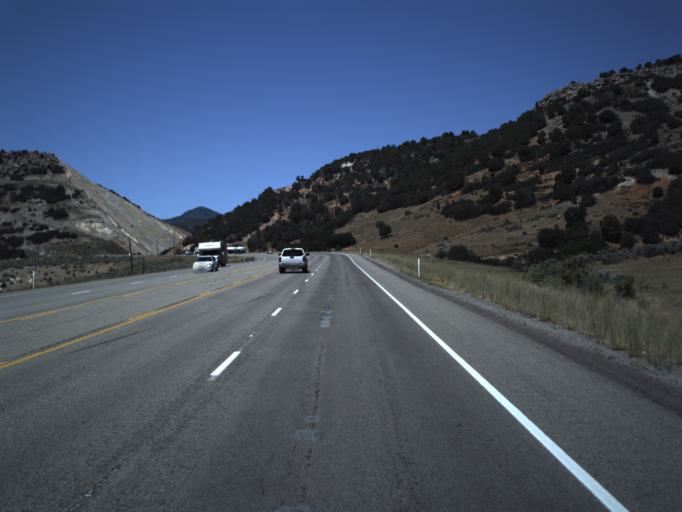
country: US
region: Utah
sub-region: Utah County
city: Mapleton
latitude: 39.9992
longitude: -111.4792
